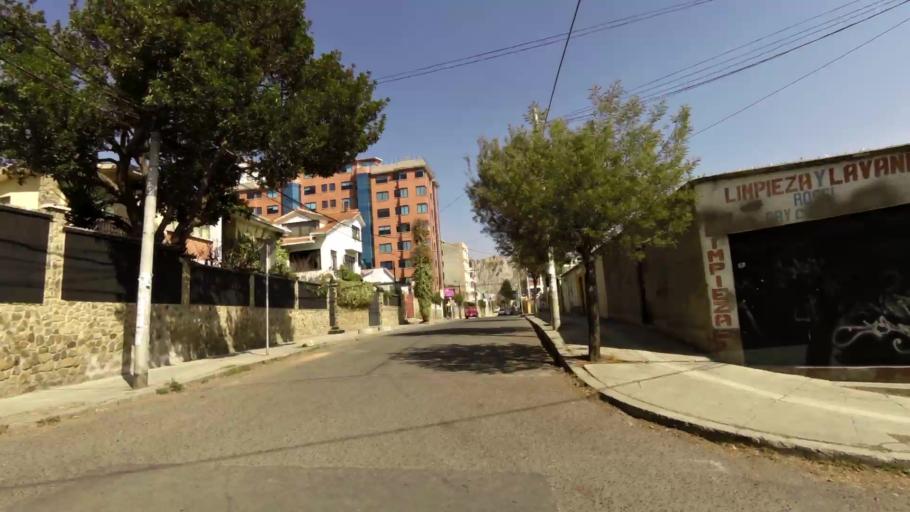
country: BO
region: La Paz
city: La Paz
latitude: -16.5371
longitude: -68.0778
